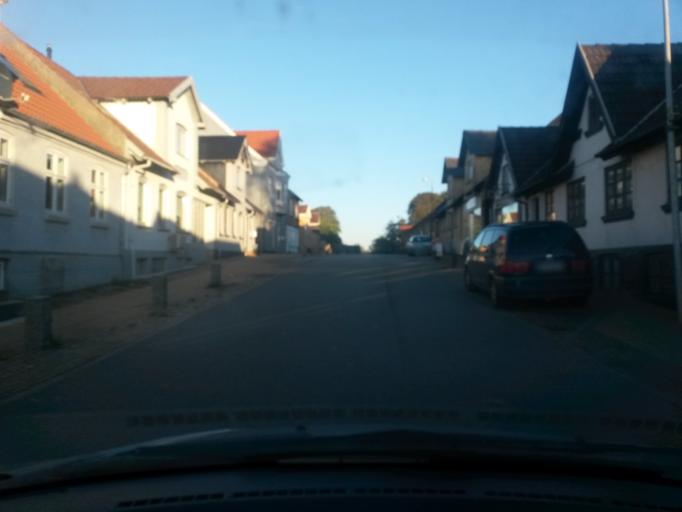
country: DK
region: Central Jutland
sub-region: Silkeborg Kommune
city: Kjellerup
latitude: 56.2861
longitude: 9.3316
